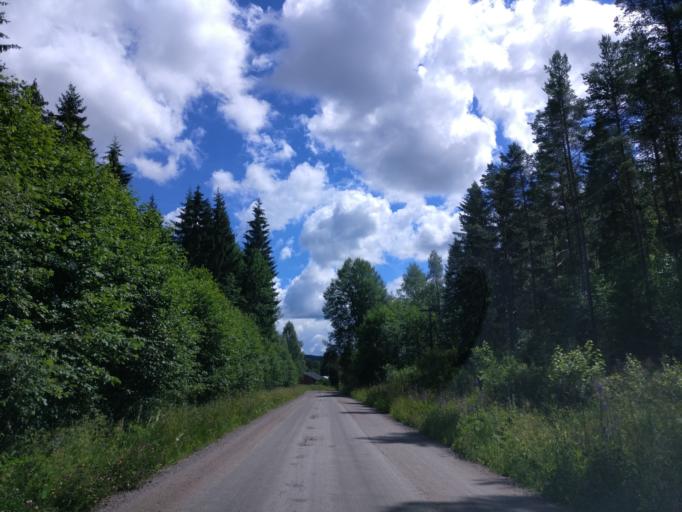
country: SE
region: Vaermland
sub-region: Hagfors Kommun
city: Hagfors
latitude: 60.0292
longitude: 13.6715
